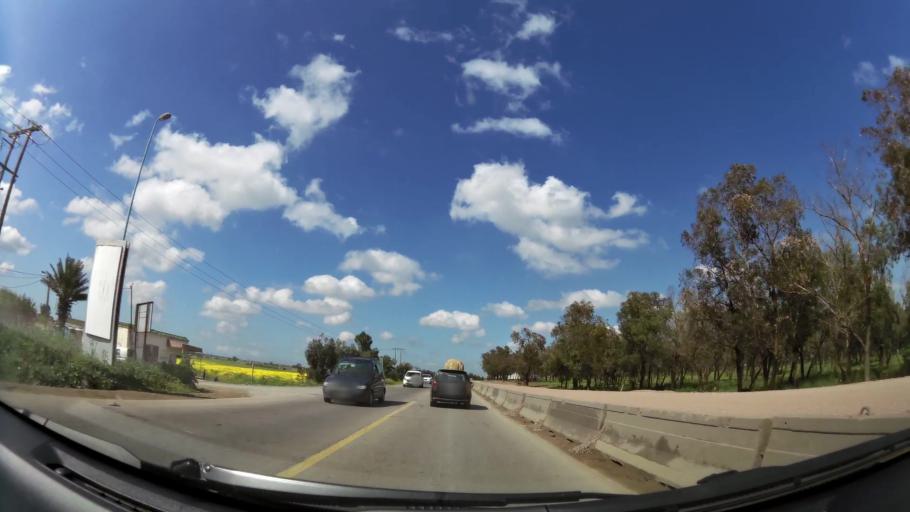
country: MA
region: Grand Casablanca
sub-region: Mediouna
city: Mediouna
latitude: 33.4122
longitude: -7.5326
